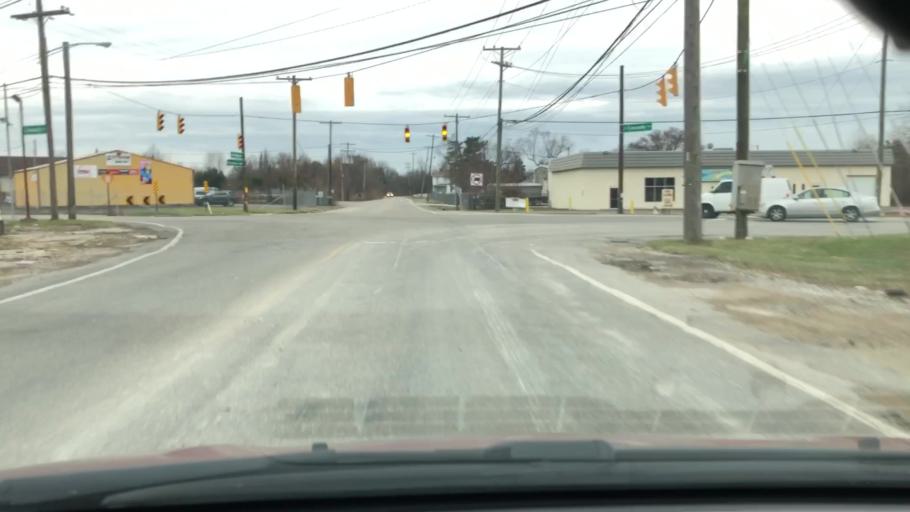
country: US
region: Ohio
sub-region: Franklin County
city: Bexley
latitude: 39.9958
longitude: -82.9299
